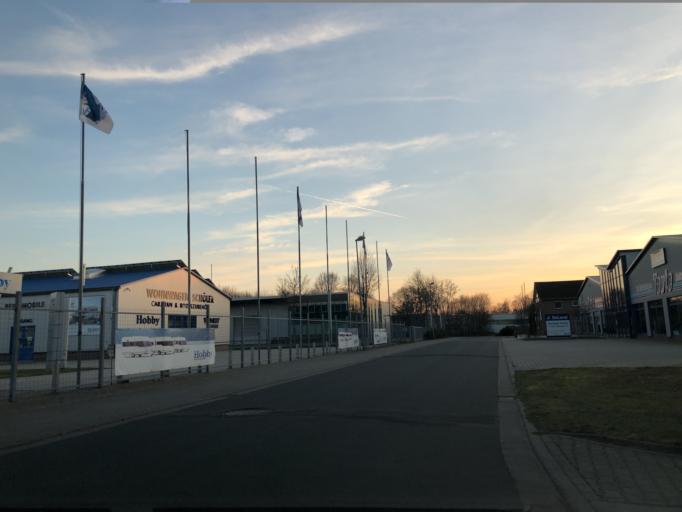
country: DE
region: Lower Saxony
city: Papenburg
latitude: 53.0959
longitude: 7.4063
